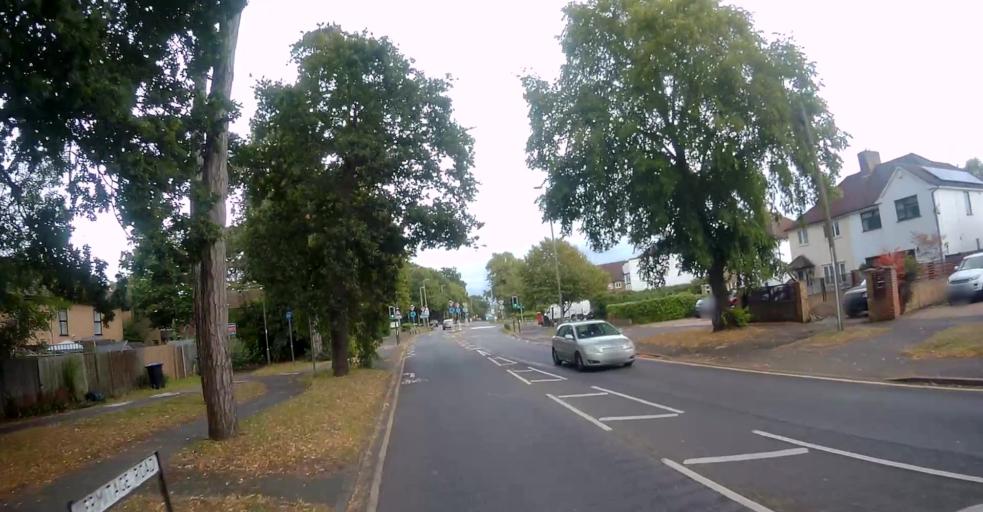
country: GB
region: England
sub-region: Surrey
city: Knaphill
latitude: 51.3127
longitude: -0.6076
